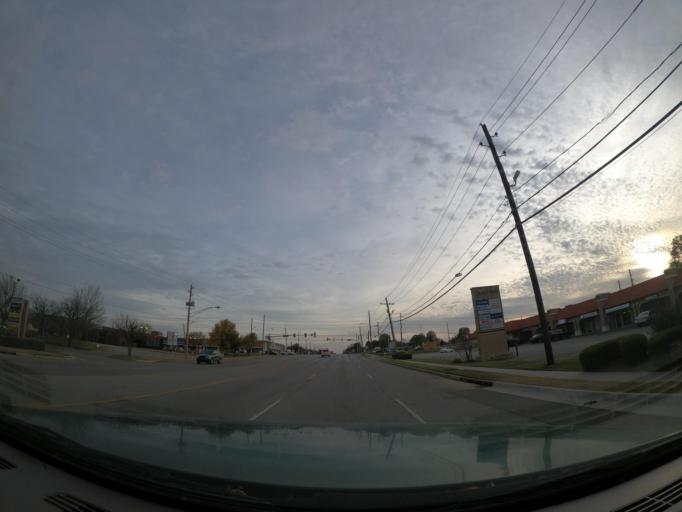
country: US
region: Oklahoma
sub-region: Tulsa County
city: Broken Arrow
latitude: 36.0474
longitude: -95.8154
